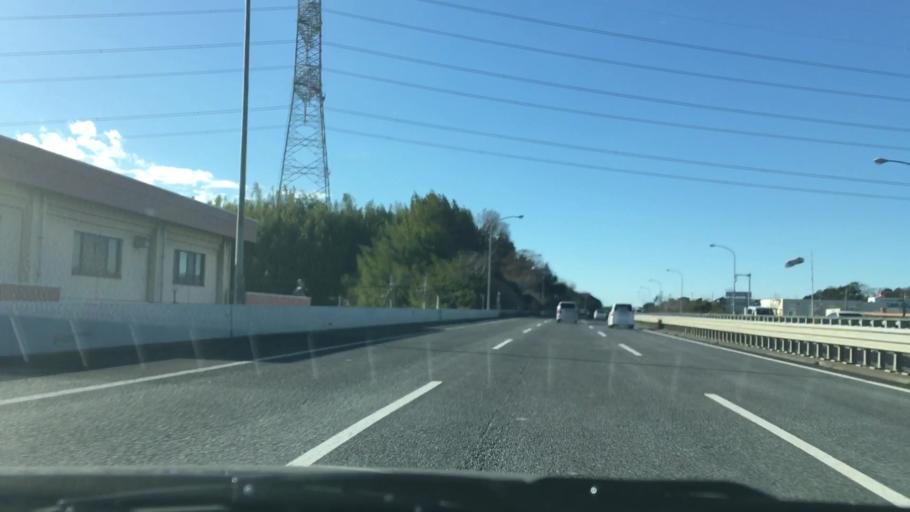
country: JP
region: Chiba
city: Yotsukaido
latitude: 35.6822
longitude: 140.1969
